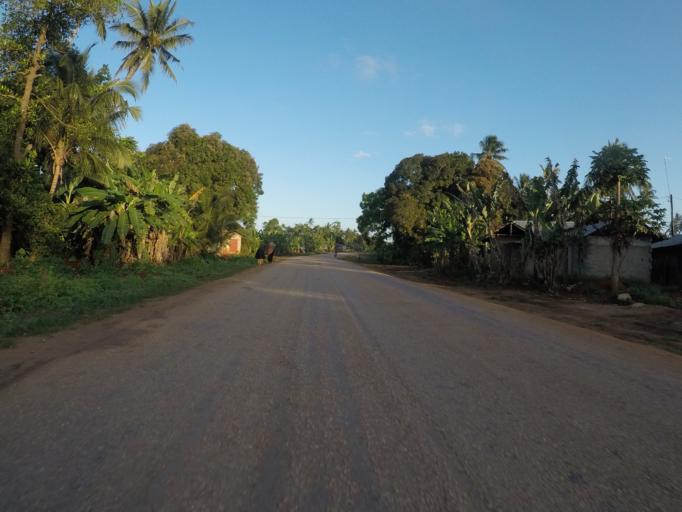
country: TZ
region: Zanzibar North
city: Gamba
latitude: -5.8934
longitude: 39.2907
